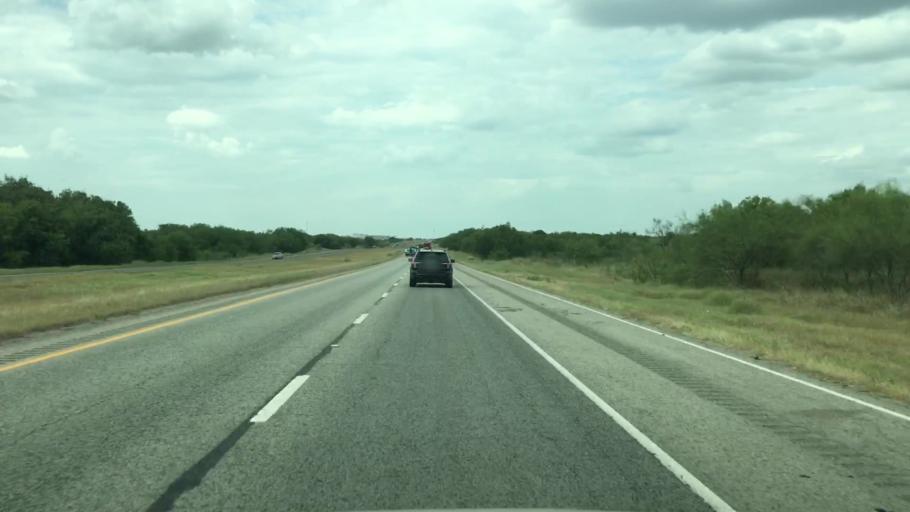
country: US
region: Texas
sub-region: Atascosa County
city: Pleasanton
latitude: 29.0754
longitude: -98.4328
